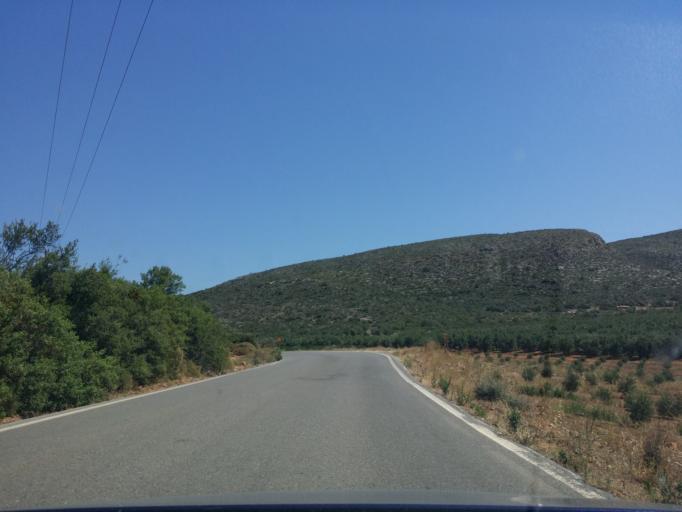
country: GR
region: Peloponnese
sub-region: Nomos Lakonias
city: Kato Glikovrisi
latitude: 36.8722
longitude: 22.8144
